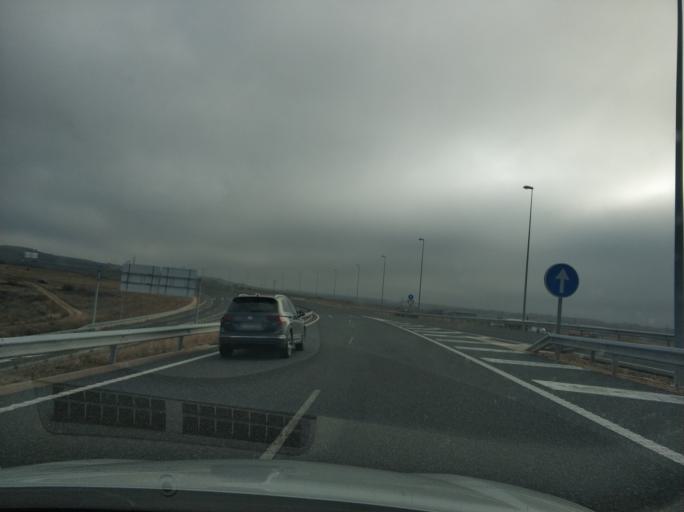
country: ES
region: Castille and Leon
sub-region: Provincia de Leon
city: Leon
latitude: 42.5690
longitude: -5.5450
